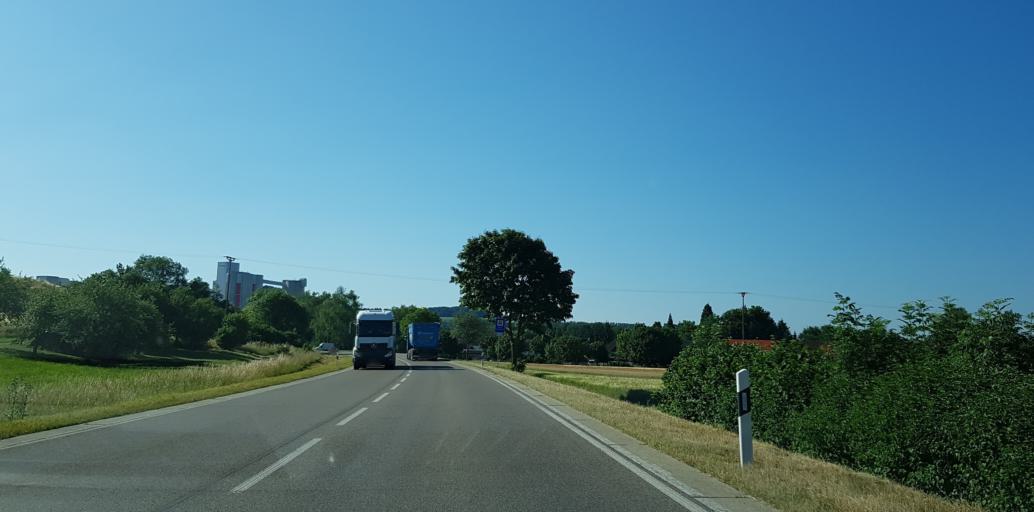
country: DE
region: Baden-Wuerttemberg
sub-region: Tuebingen Region
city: Allmendingen
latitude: 48.3378
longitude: 9.7227
